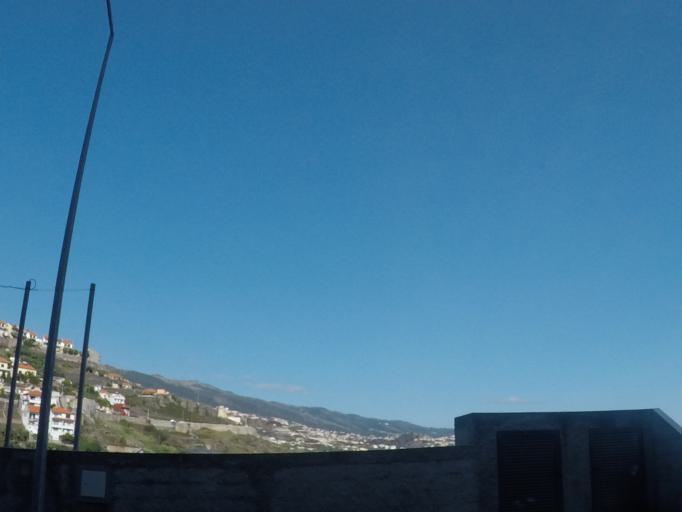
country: PT
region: Madeira
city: Camara de Lobos
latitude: 32.6553
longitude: -16.9902
